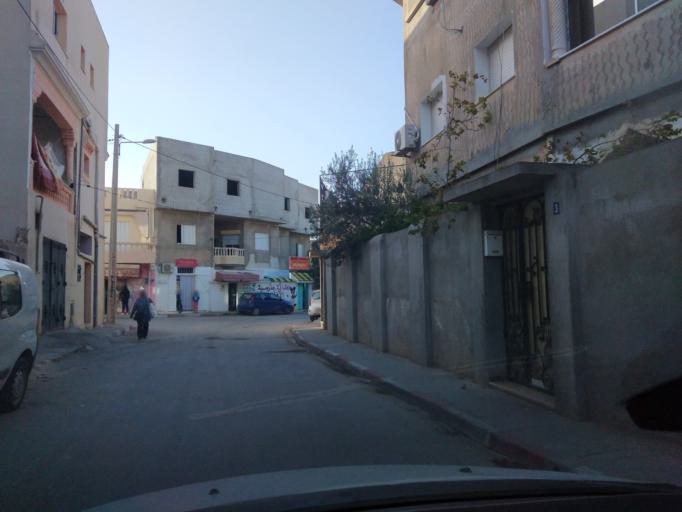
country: TN
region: Manouba
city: Manouba
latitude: 36.7928
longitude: 10.0886
